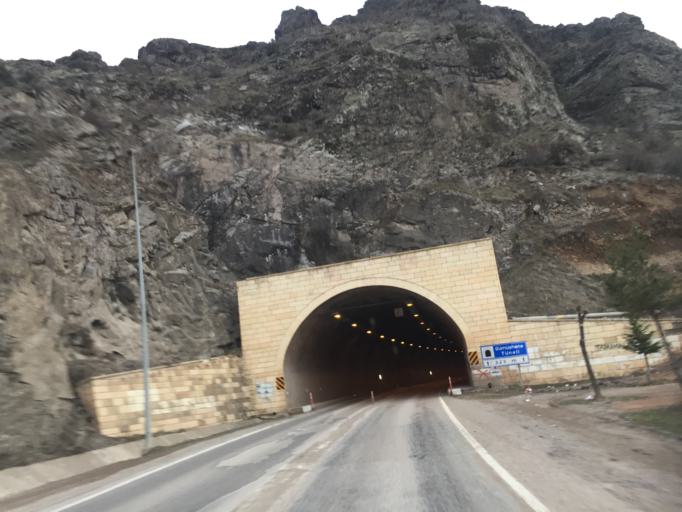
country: TR
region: Gumushane
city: Gumushkhane
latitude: 40.4731
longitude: 39.4644
